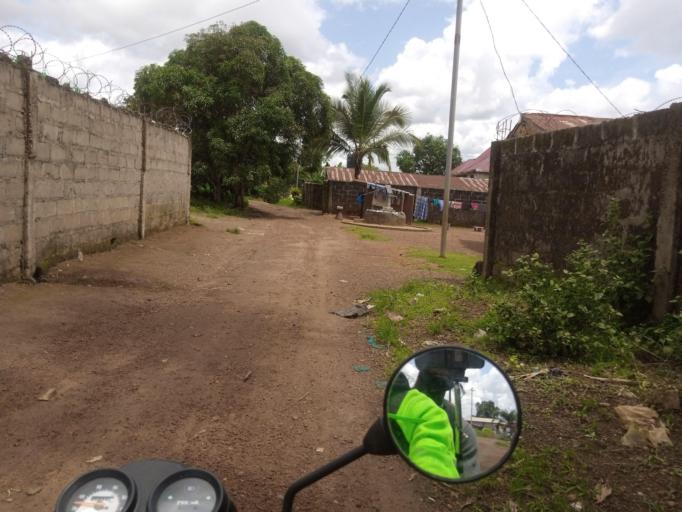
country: SL
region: Northern Province
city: Port Loko
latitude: 8.7596
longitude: -12.7791
